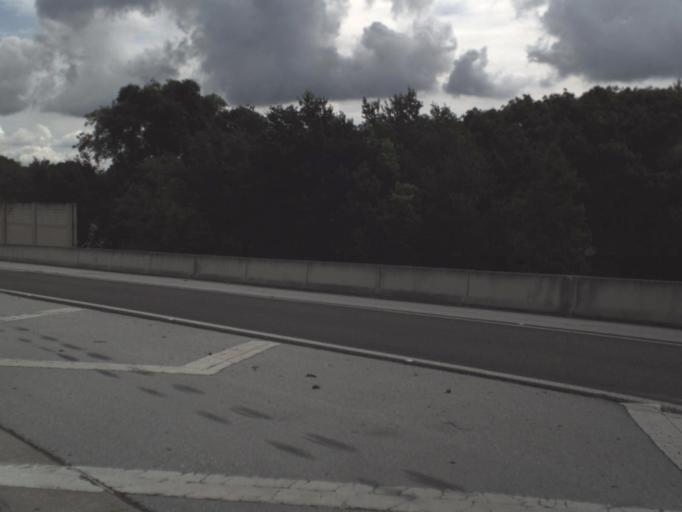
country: US
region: Florida
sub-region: Polk County
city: Gibsonia
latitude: 28.0873
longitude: -81.9669
